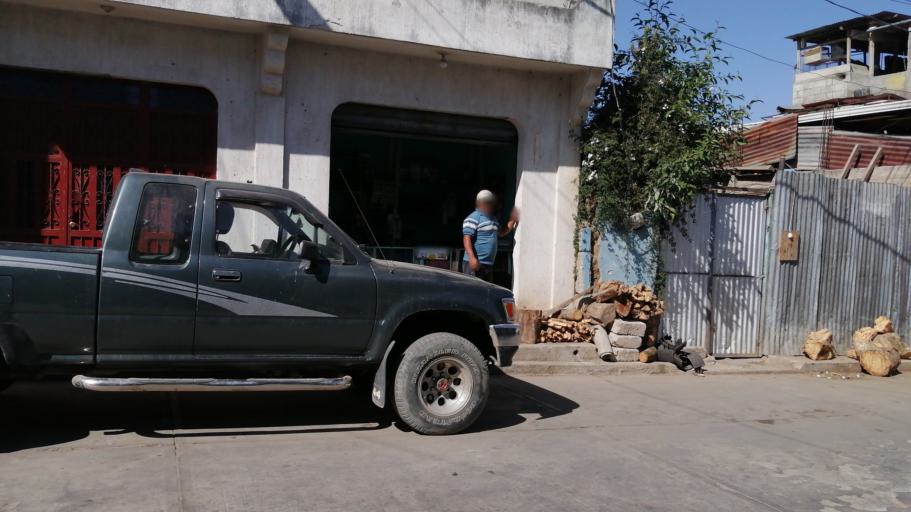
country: GT
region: Quetzaltenango
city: Ostuncalco
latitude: 14.8693
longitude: -91.6255
